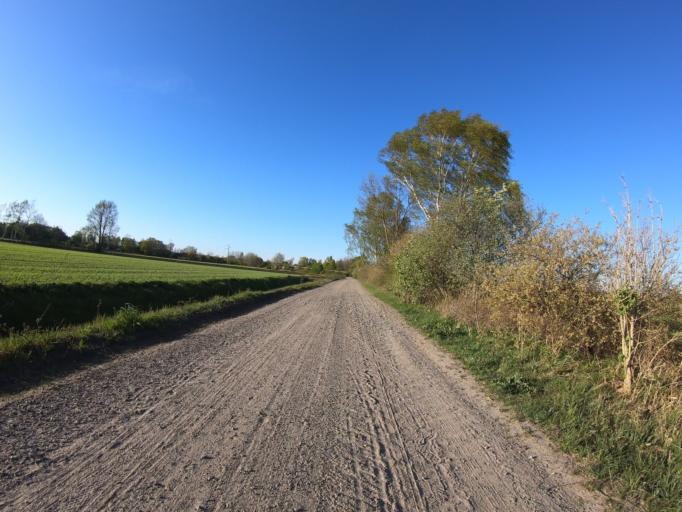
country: DE
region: Lower Saxony
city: Wagenhoff
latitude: 52.5103
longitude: 10.5200
